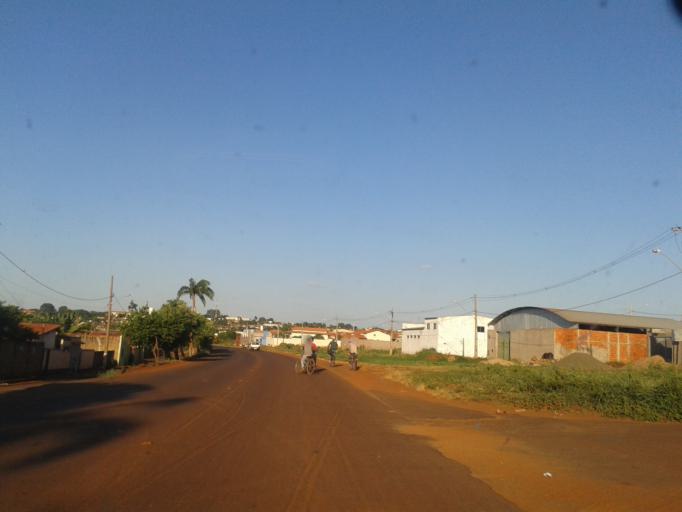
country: BR
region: Minas Gerais
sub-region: Capinopolis
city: Capinopolis
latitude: -18.6869
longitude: -49.5800
